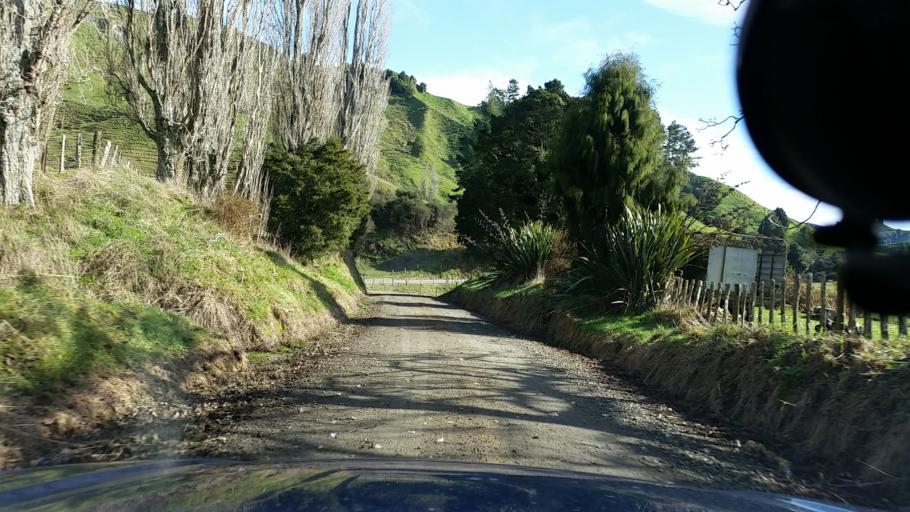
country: NZ
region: Taranaki
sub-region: New Plymouth District
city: Waitara
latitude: -39.0576
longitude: 174.7760
